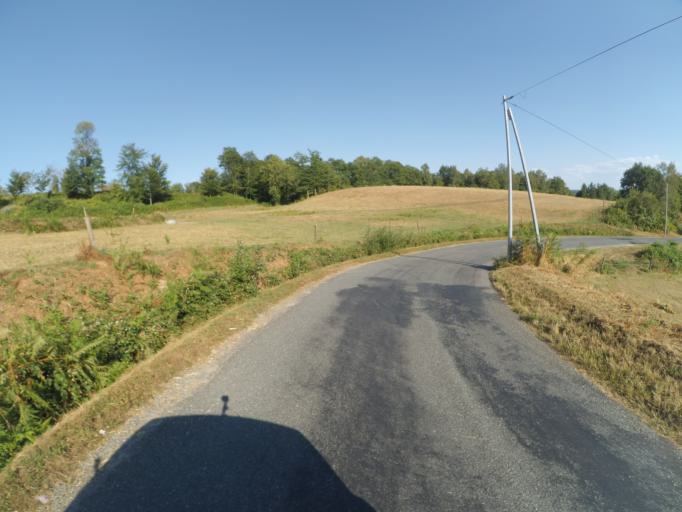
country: FR
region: Limousin
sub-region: Departement de la Haute-Vienne
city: Peyrat-le-Chateau
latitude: 45.7560
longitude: 1.8165
